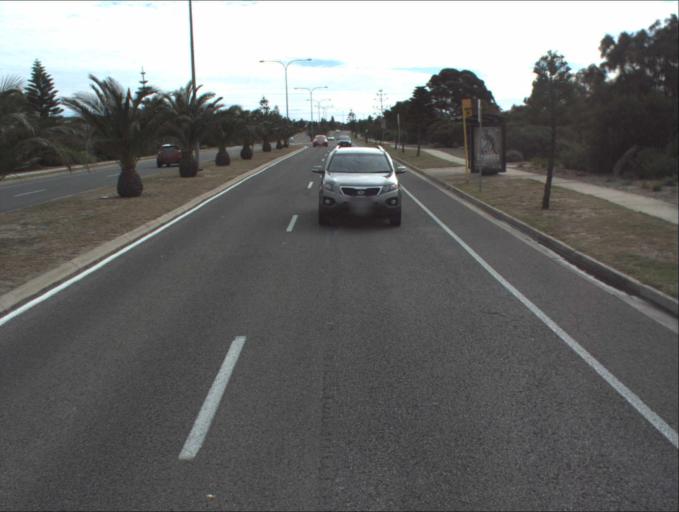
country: AU
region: South Australia
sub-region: Charles Sturt
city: West Lakes Shore
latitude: -34.8704
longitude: 138.4817
